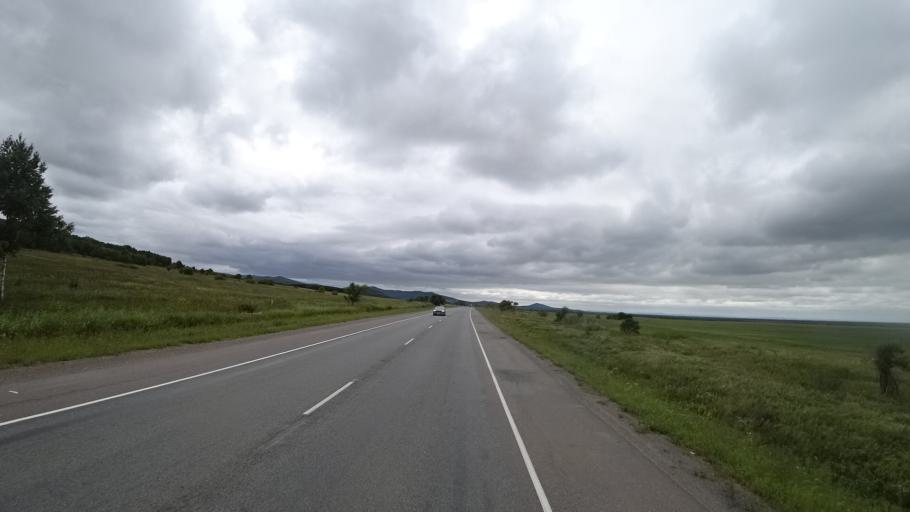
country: RU
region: Primorskiy
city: Chernigovka
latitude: 44.3044
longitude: 132.5358
